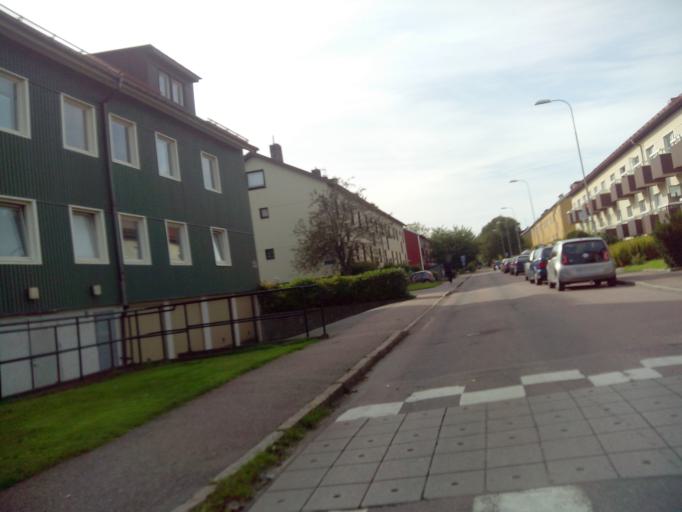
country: SE
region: Vaestra Goetaland
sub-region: Goteborg
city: Goeteborg
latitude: 57.7268
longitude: 11.9444
